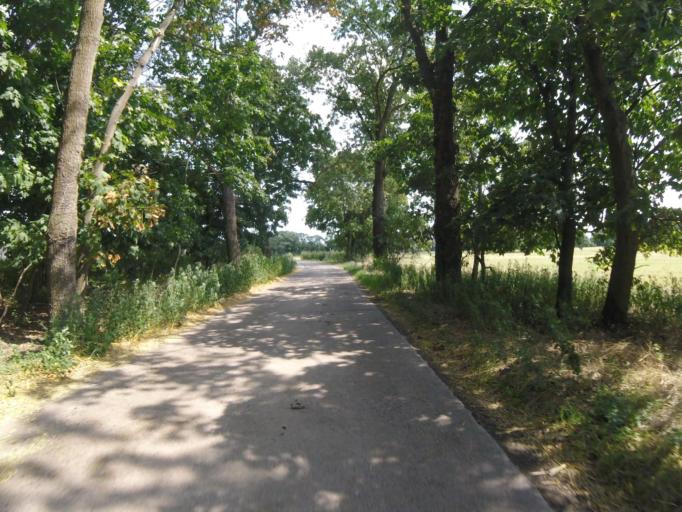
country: DE
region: Brandenburg
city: Mittenwalde
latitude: 52.2722
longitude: 13.5162
